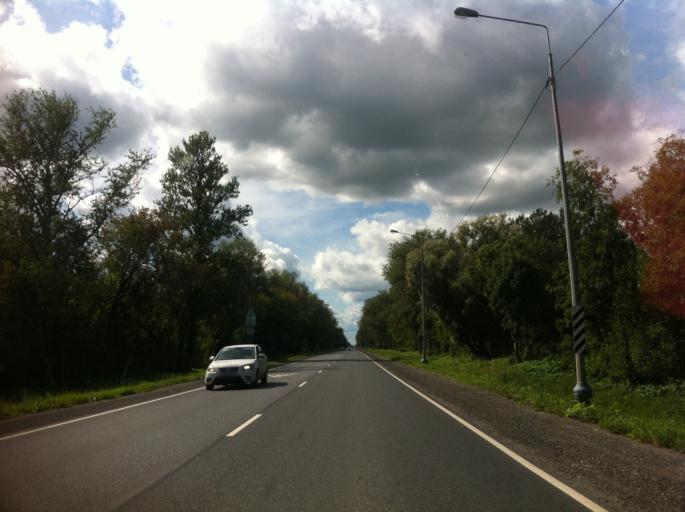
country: RU
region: Pskov
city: Pskov
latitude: 57.7787
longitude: 28.1582
